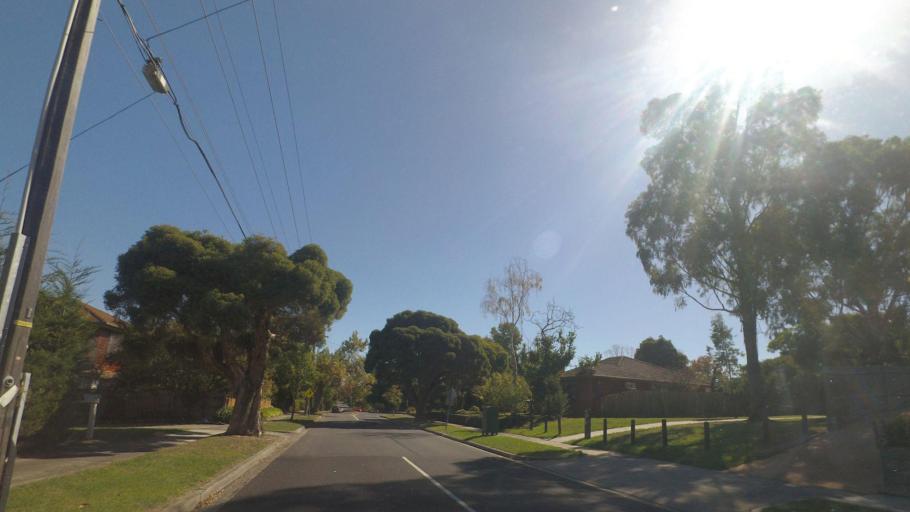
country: AU
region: Victoria
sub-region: Manningham
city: Donvale
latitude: -37.7978
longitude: 145.1746
